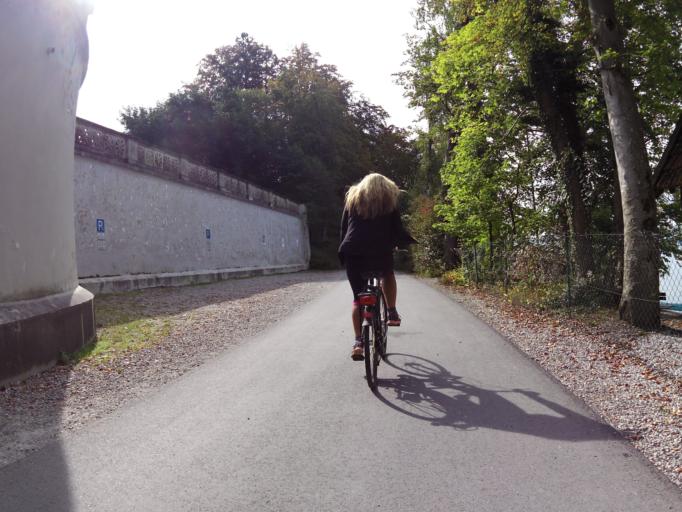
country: DE
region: Bavaria
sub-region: Upper Bavaria
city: Berg
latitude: 47.9387
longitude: 11.3370
